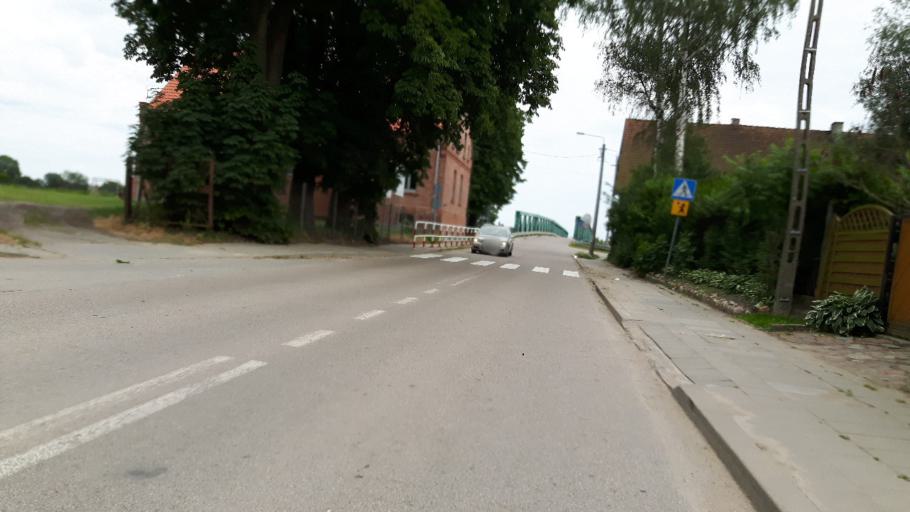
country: PL
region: Warmian-Masurian Voivodeship
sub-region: Powiat elblaski
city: Elblag
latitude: 54.1904
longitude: 19.3132
